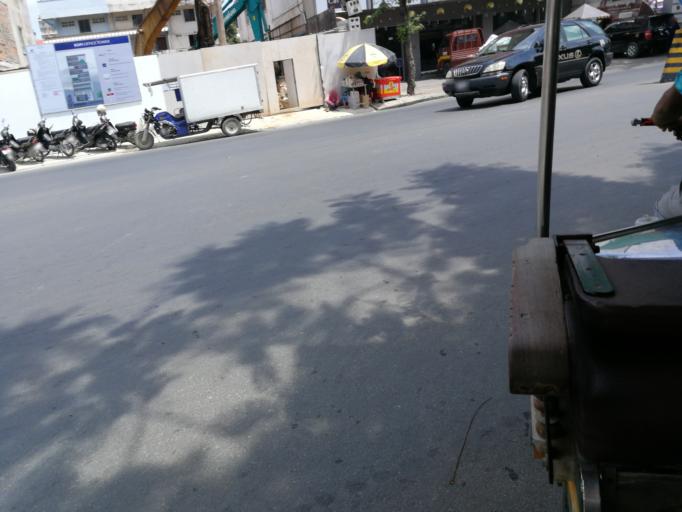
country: KH
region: Phnom Penh
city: Phnom Penh
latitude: 11.5445
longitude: 104.9180
